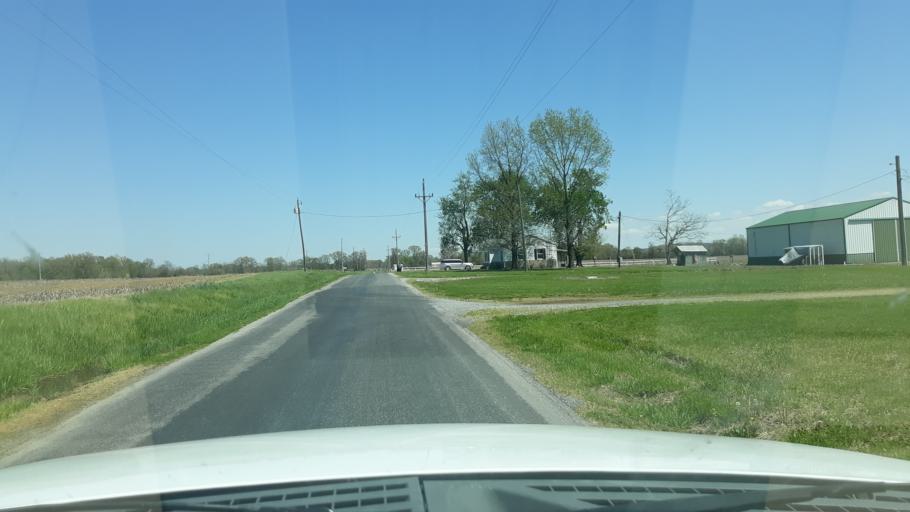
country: US
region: Illinois
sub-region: Saline County
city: Harrisburg
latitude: 37.8342
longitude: -88.6369
